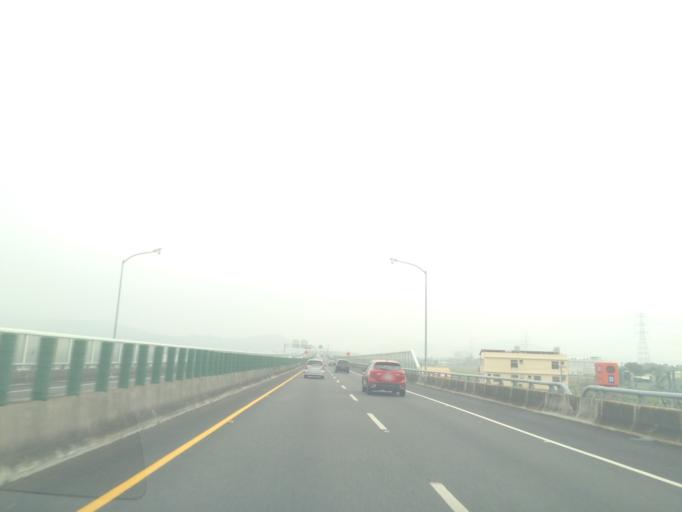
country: TW
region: Taiwan
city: Zhongxing New Village
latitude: 24.0254
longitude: 120.6721
